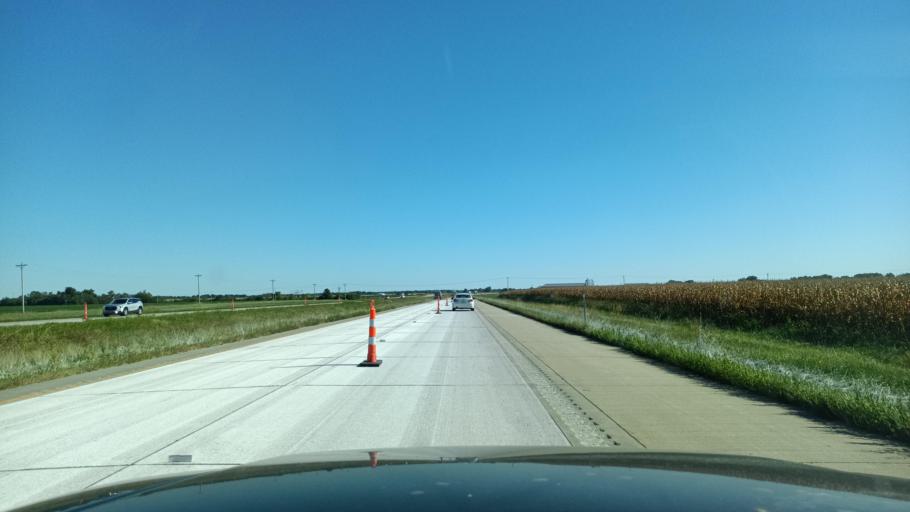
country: US
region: Missouri
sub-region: Randolph County
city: Moberly
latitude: 39.5227
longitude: -92.4384
